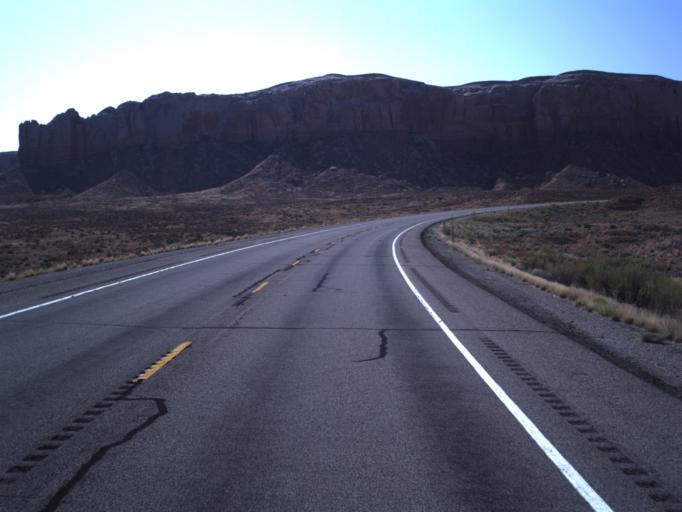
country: US
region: Utah
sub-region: San Juan County
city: Blanding
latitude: 37.2457
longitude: -109.6083
